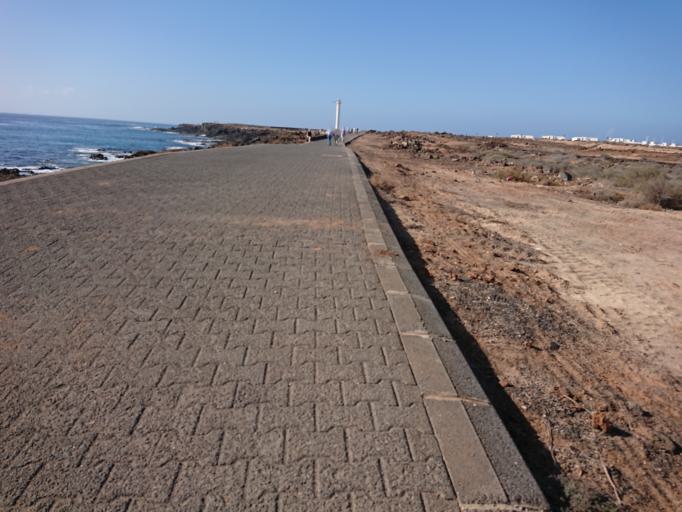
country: ES
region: Canary Islands
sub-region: Provincia de Las Palmas
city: Playa Blanca
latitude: 28.8593
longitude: -13.8655
